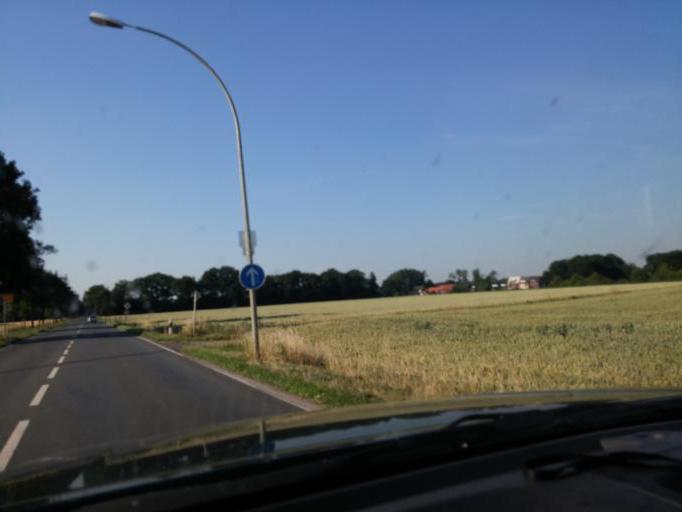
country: DE
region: North Rhine-Westphalia
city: Wegberg
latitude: 51.1727
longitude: 6.3415
